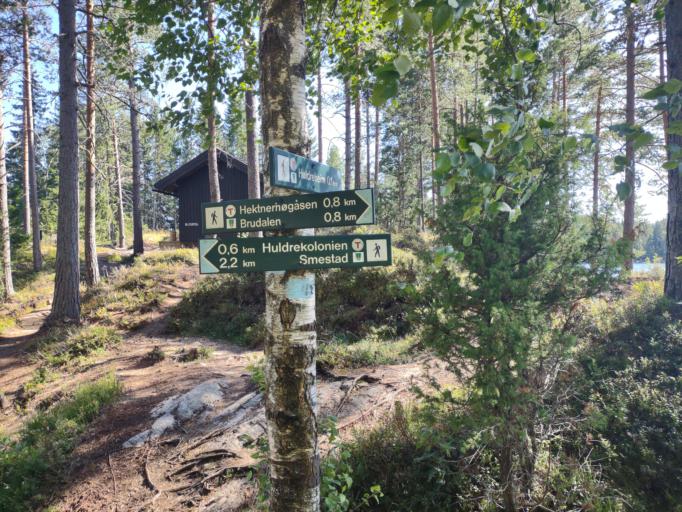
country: NO
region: Akershus
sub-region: Raelingen
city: Fjerdingby
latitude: 59.8895
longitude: 11.0609
